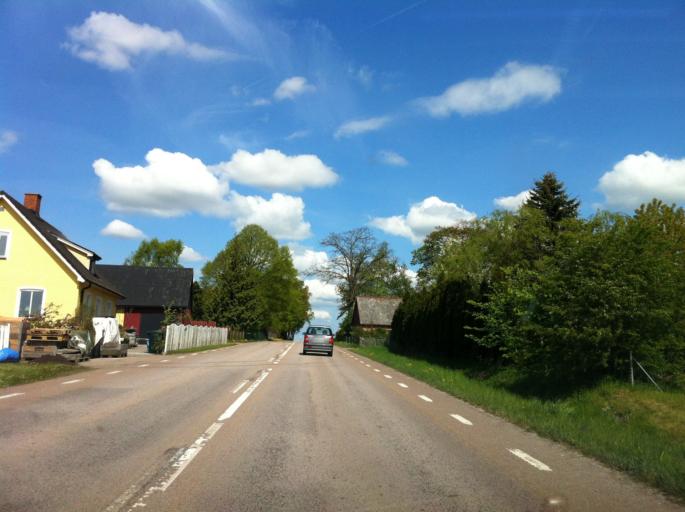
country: SE
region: Skane
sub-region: Landskrona
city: Asmundtorp
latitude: 55.9353
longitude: 12.9508
